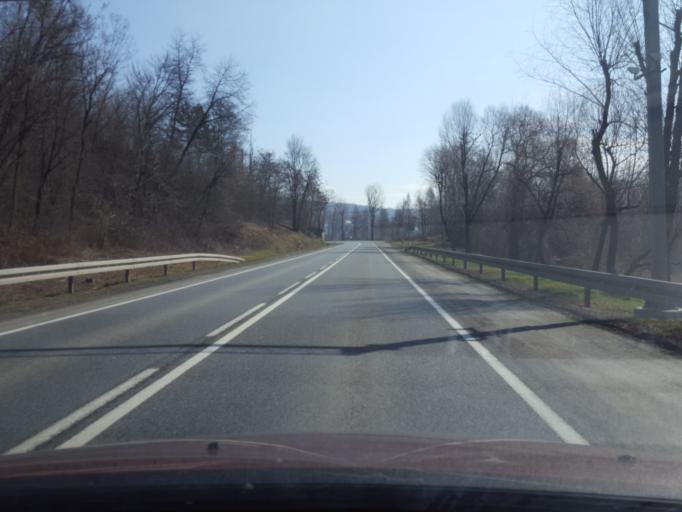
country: PL
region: Lesser Poland Voivodeship
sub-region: Powiat nowosadecki
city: Chelmiec
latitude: 49.6755
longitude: 20.6630
